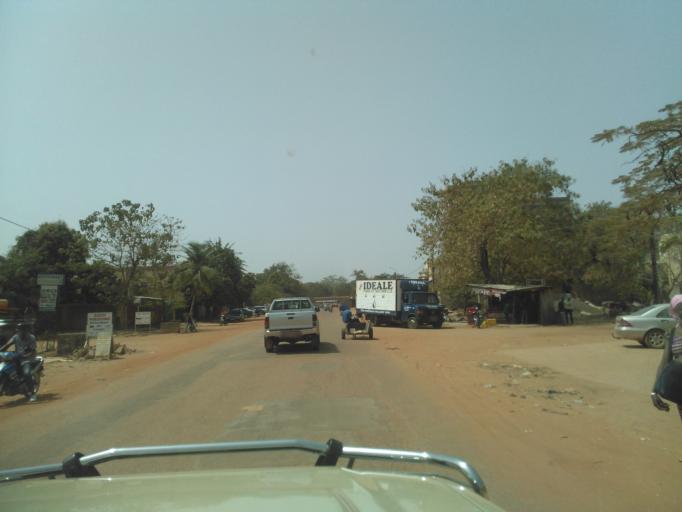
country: BF
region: Centre
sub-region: Kadiogo Province
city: Ouagadougou
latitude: 12.3818
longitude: -1.4873
